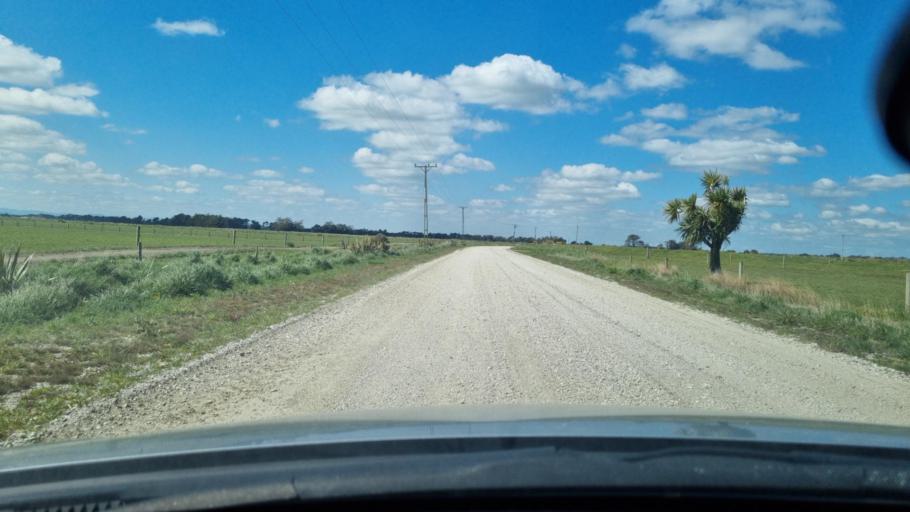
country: NZ
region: Southland
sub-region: Invercargill City
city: Invercargill
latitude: -46.3914
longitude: 168.2548
